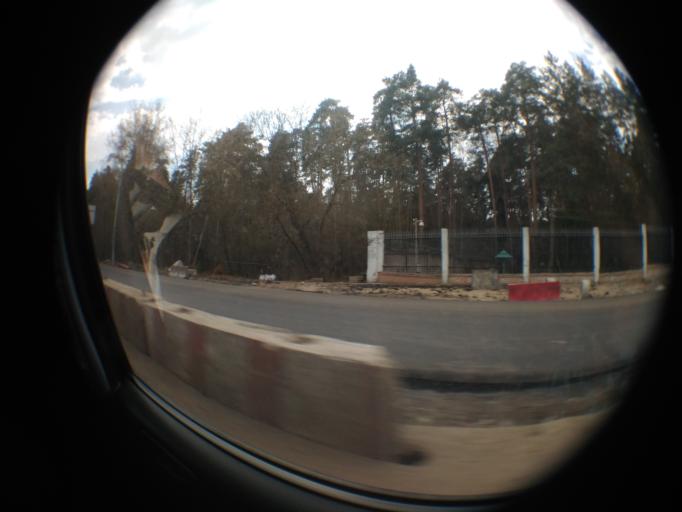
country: RU
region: Moskovskaya
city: Zhukovskiy
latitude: 55.5879
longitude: 38.1195
